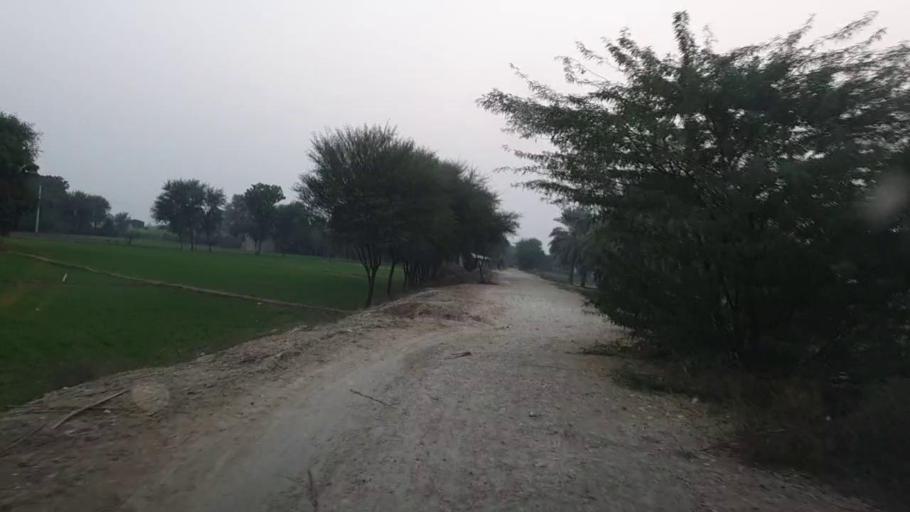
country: PK
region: Sindh
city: Kandiari
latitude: 26.9631
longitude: 68.4652
